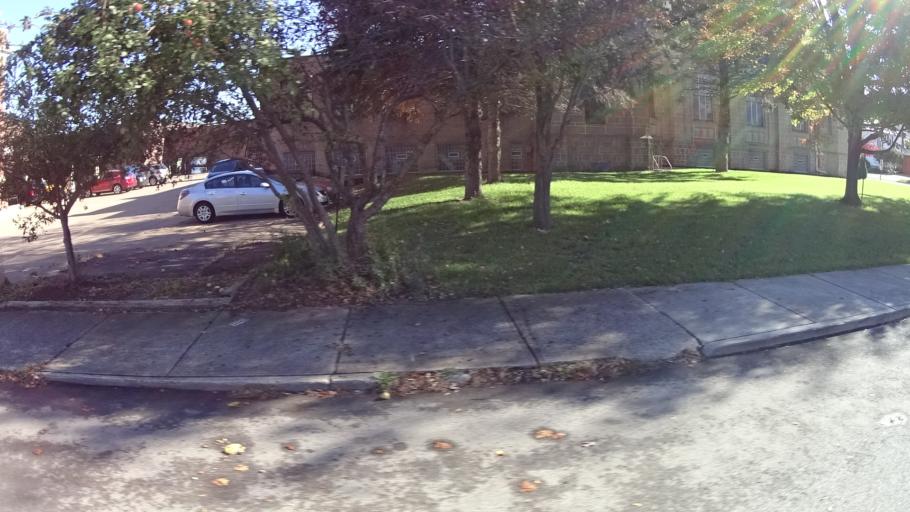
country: US
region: Ohio
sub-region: Lorain County
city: Lorain
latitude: 41.4659
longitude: -82.1799
